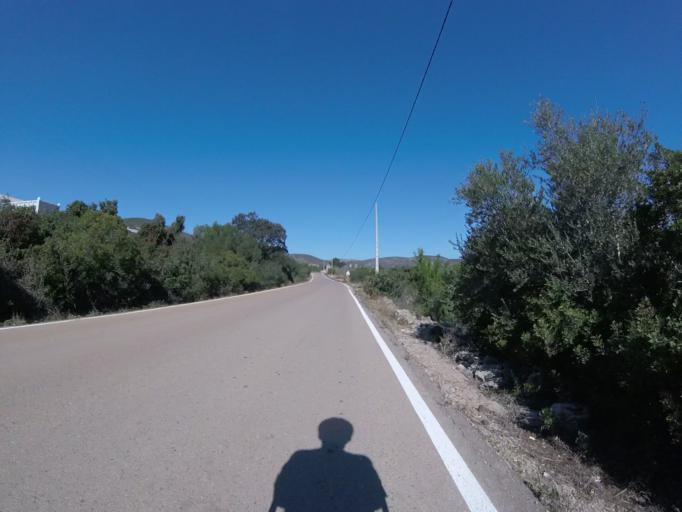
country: ES
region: Valencia
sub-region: Provincia de Castello
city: Santa Magdalena de Pulpis
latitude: 40.3628
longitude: 0.2809
